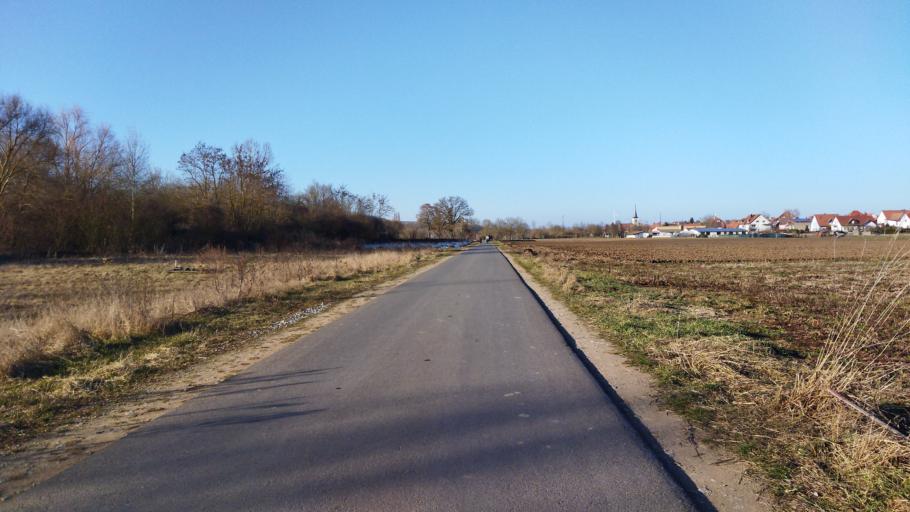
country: DE
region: Bavaria
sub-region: Regierungsbezirk Unterfranken
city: Albertshofen
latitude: 49.7634
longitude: 10.1581
